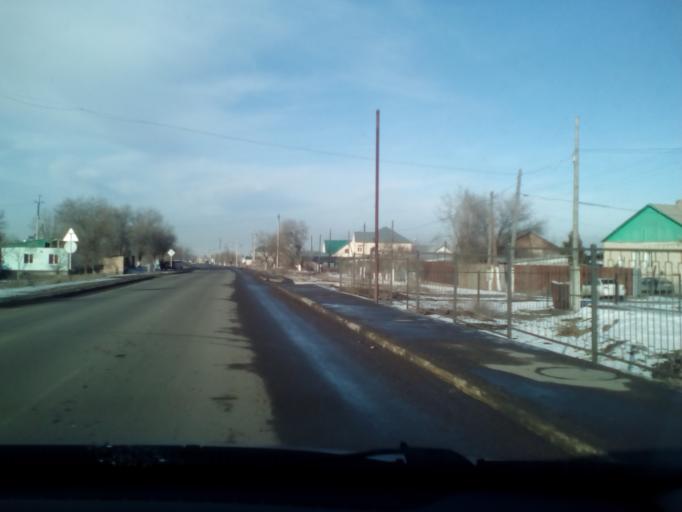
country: KZ
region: Almaty Oblysy
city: Burunday
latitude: 43.1855
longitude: 76.4147
